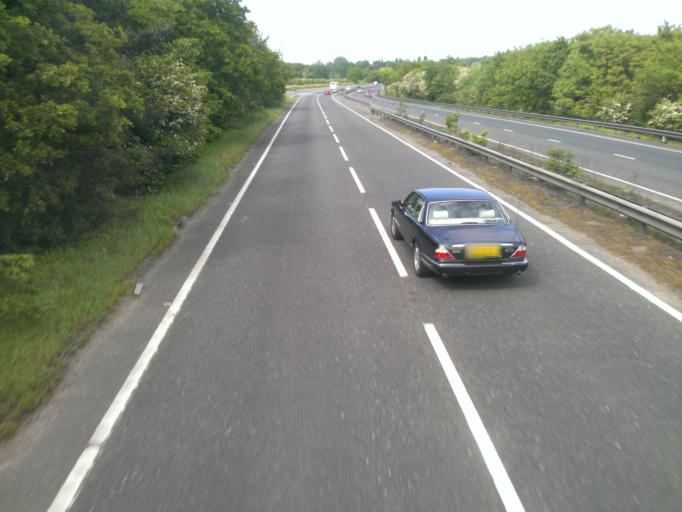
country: GB
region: England
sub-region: Essex
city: Colchester
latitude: 51.9298
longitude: 0.9434
